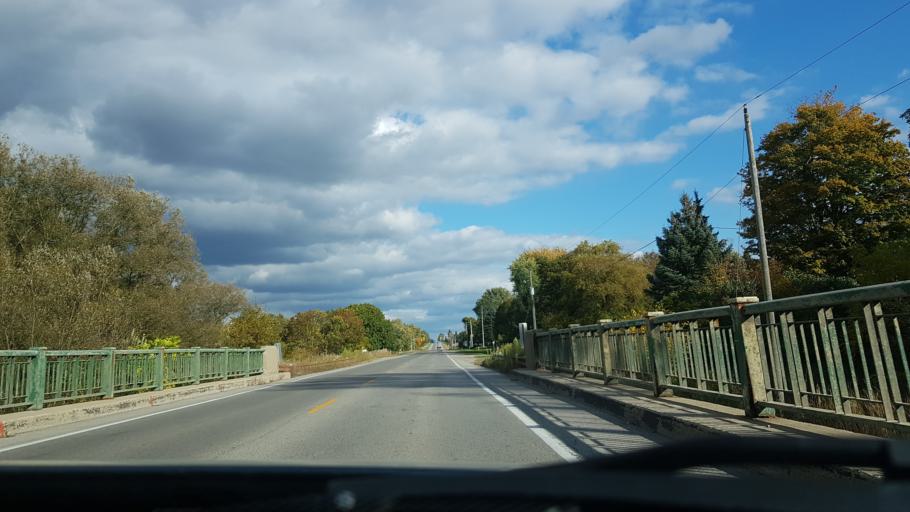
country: CA
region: Ontario
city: Delaware
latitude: 42.9995
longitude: -81.3998
